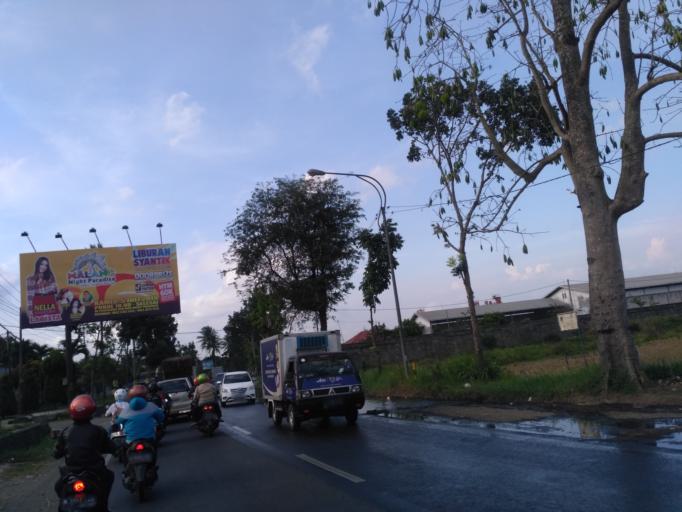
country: ID
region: East Java
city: Wadung
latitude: -8.0410
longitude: 112.6090
